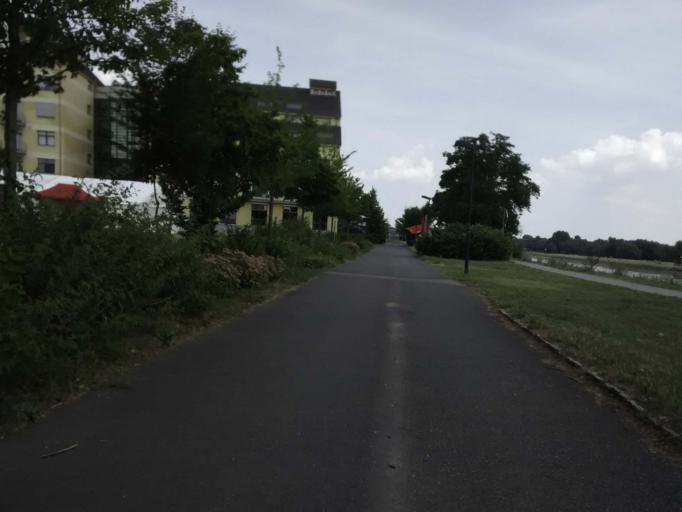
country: DE
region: Saxony-Anhalt
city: Neue Neustadt
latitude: 52.1413
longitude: 11.6576
